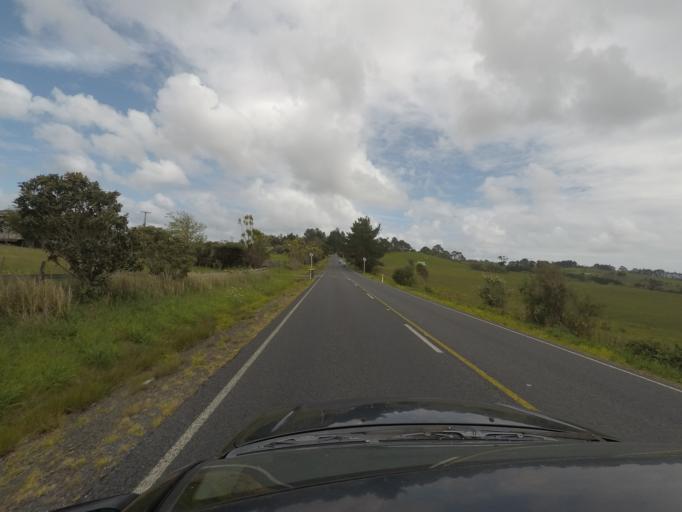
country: NZ
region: Auckland
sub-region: Auckland
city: Parakai
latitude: -36.6348
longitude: 174.5050
